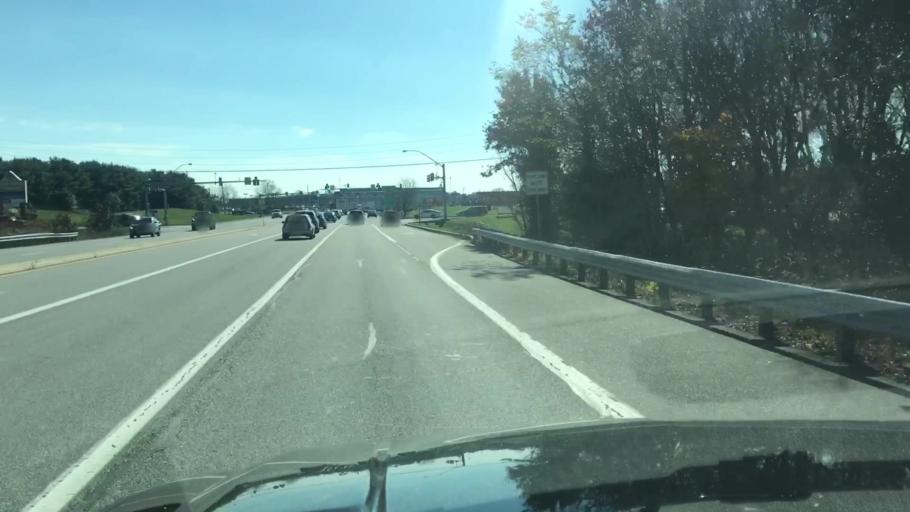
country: US
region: Pennsylvania
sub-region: Cumberland County
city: Mechanicsburg
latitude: 40.2496
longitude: -77.0295
